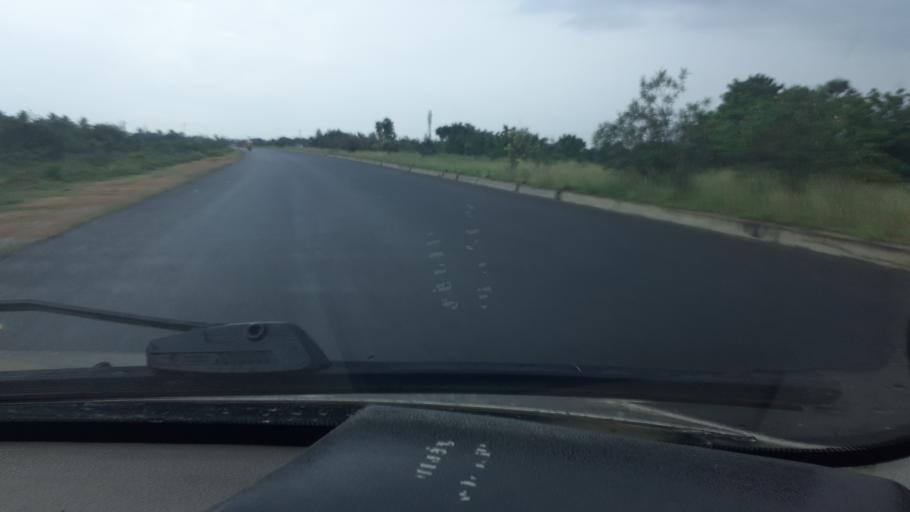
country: IN
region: Tamil Nadu
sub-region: Thoothukkudi
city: Kadambur
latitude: 9.0539
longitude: 77.7961
